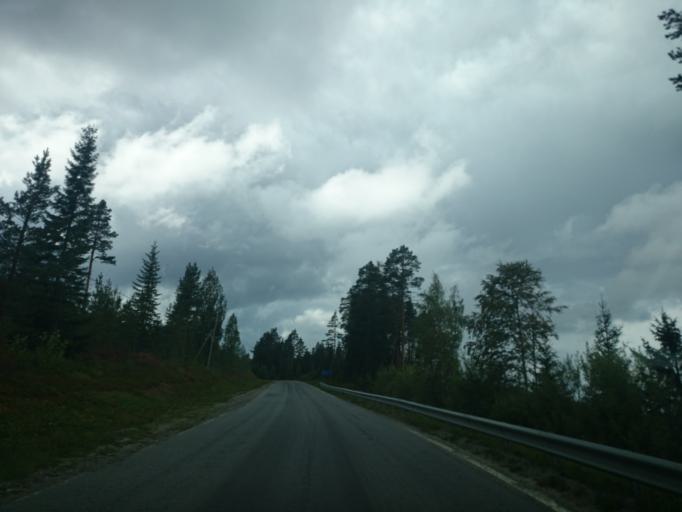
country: SE
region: Jaemtland
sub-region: Bergs Kommun
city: Hoverberg
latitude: 62.4649
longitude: 14.5220
